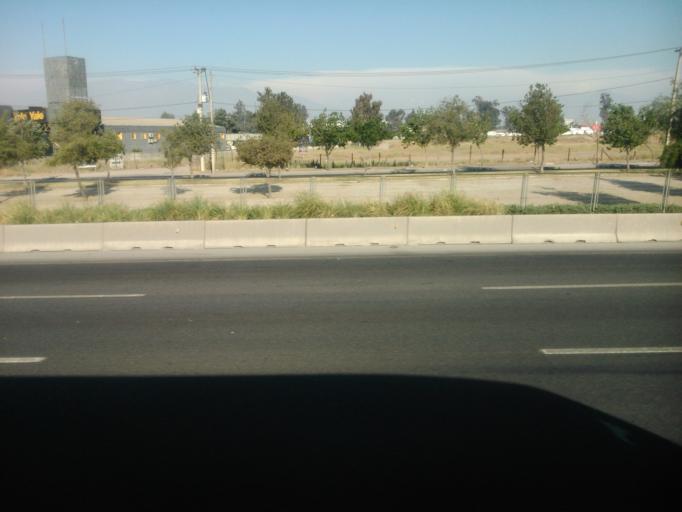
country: CL
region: Santiago Metropolitan
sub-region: Provincia de Maipo
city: San Bernardo
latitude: -33.5479
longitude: -70.7086
